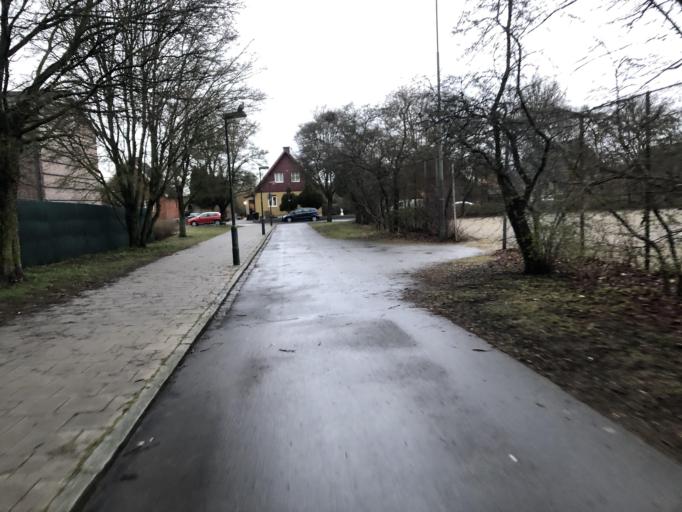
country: SE
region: Skane
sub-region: Burlovs Kommun
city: Arloev
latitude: 55.5845
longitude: 13.0617
